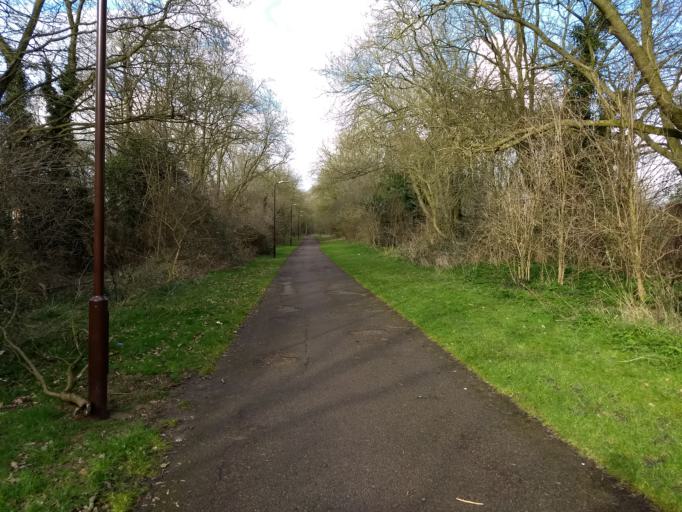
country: GB
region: England
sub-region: Milton Keynes
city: Milton Keynes
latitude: 52.0219
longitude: -0.7510
